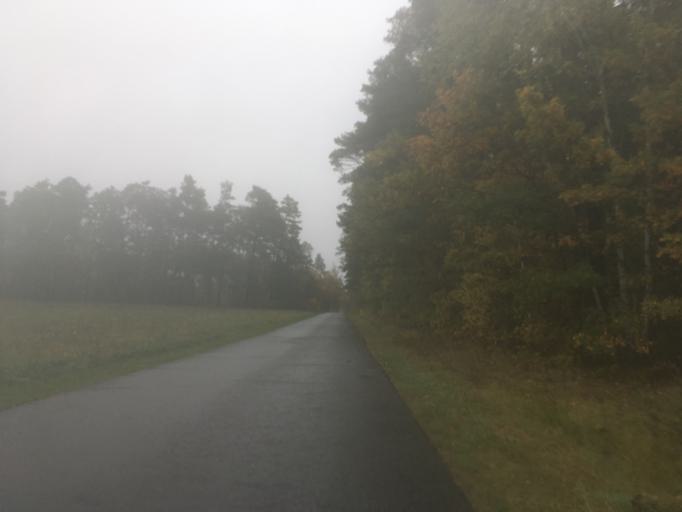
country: DE
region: Brandenburg
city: Neu Zauche
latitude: 52.0307
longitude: 14.0331
